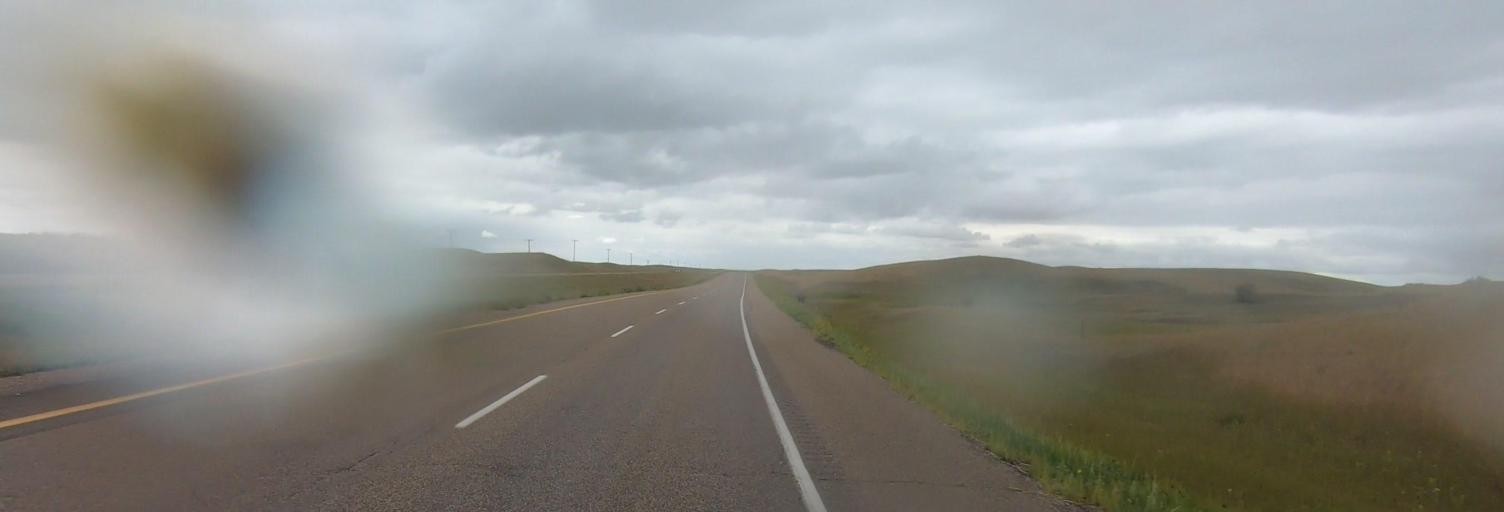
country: CA
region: Saskatchewan
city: Gravelbourg
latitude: 50.4630
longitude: -106.4773
